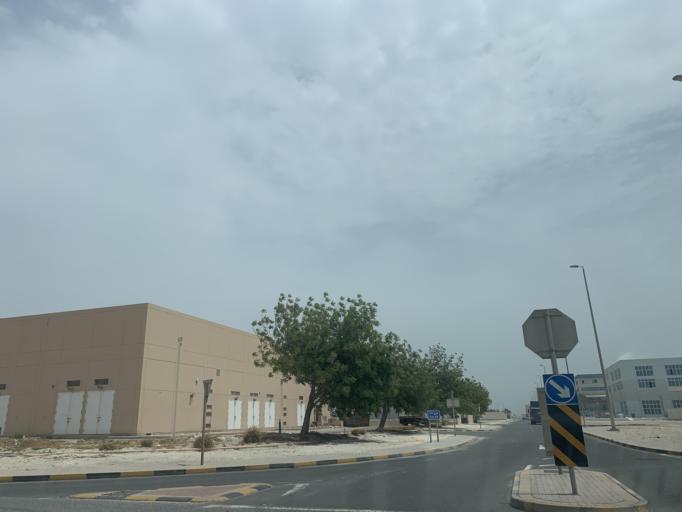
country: BH
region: Muharraq
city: Al Hadd
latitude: 26.2181
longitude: 50.6741
